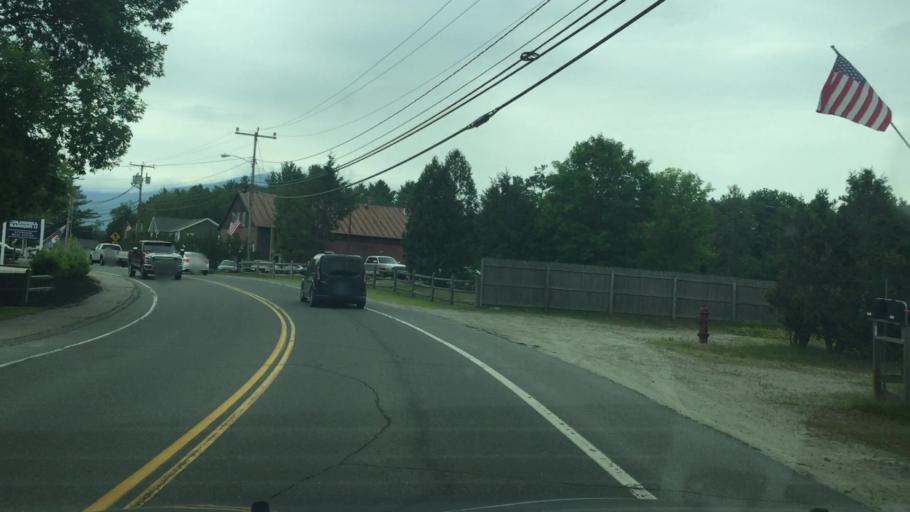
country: US
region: New Hampshire
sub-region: Grafton County
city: Littleton
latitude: 44.2295
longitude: -71.7537
